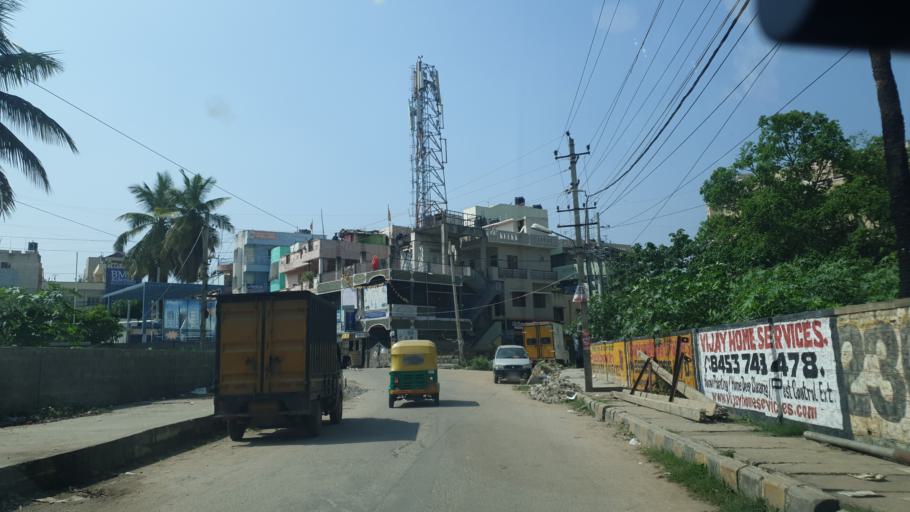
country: IN
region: Karnataka
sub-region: Bangalore Urban
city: Bangalore
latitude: 12.9778
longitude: 77.6663
